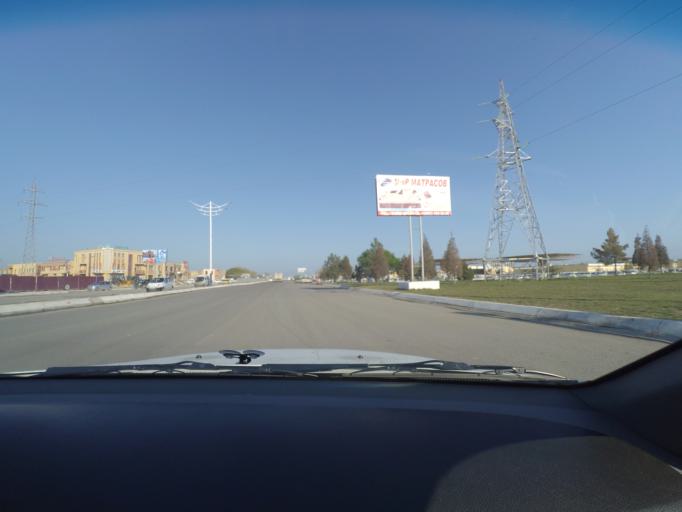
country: UZ
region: Bukhara
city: Bukhara
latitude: 39.8034
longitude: 64.4275
